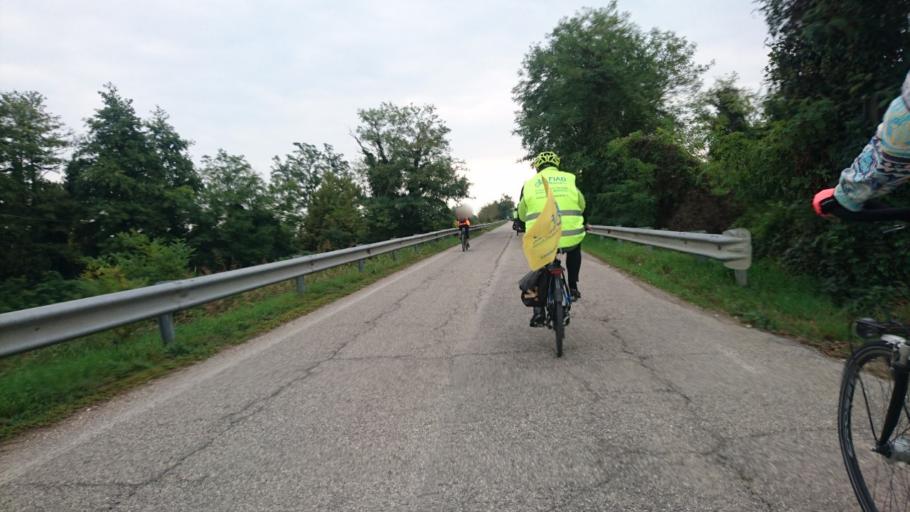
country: IT
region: Veneto
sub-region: Provincia di Verona
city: San Martino Buon Albergo
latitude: 45.4060
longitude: 11.0639
